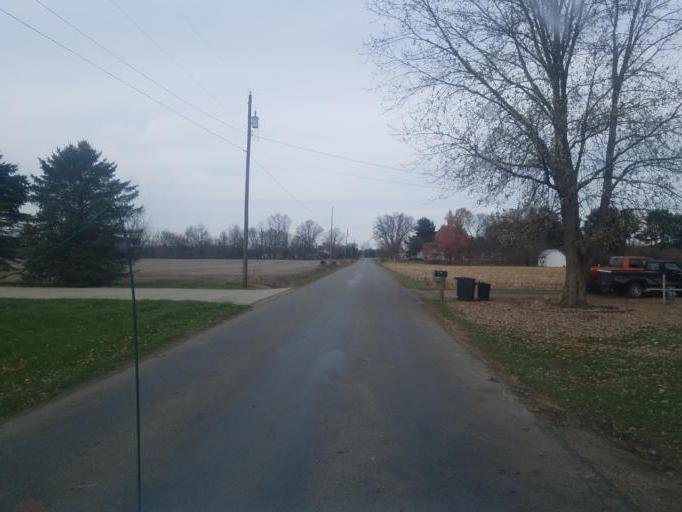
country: US
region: Ohio
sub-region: Knox County
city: Mount Vernon
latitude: 40.3985
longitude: -82.5128
